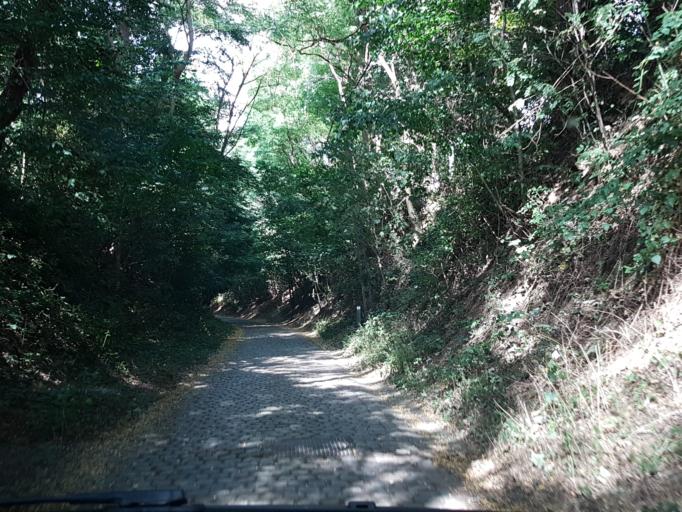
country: BE
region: Flanders
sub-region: Provincie Vlaams-Brabant
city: Herent
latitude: 50.8965
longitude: 4.6651
